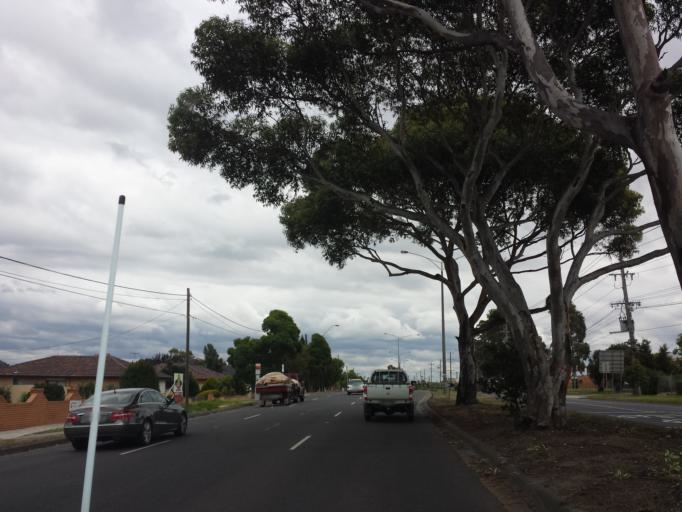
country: AU
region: Victoria
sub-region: Whittlesea
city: Thomastown
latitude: -37.6937
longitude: 144.9992
